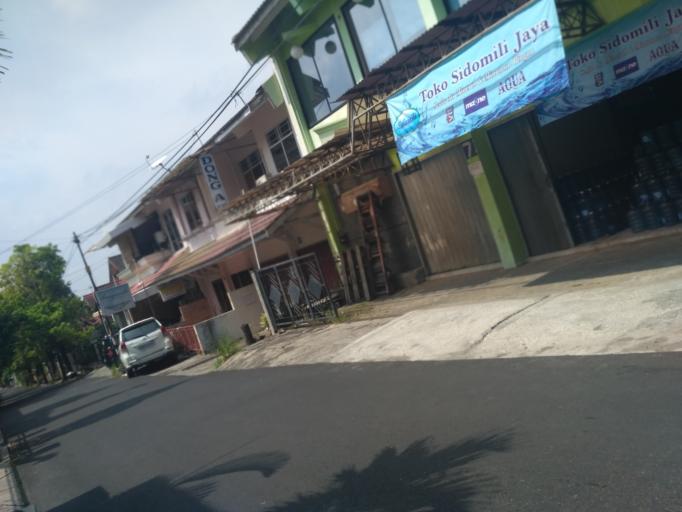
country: ID
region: Central Java
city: Semarang
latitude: -7.0478
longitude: 110.4250
